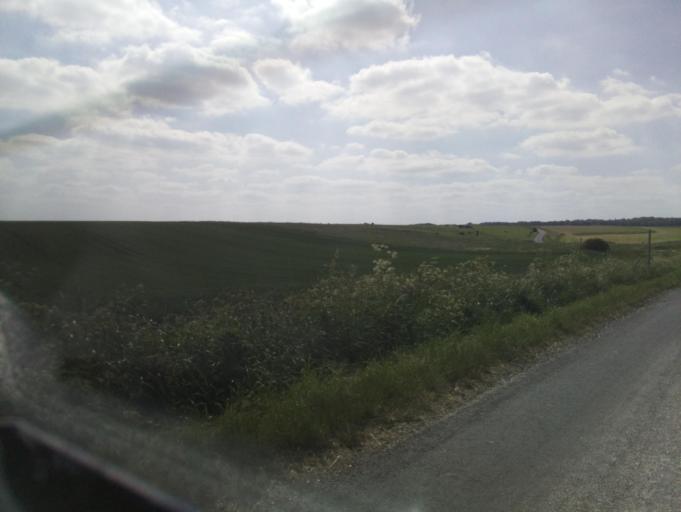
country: GB
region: England
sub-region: Wiltshire
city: Collingbourne Kingston
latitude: 51.2820
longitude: -1.6798
